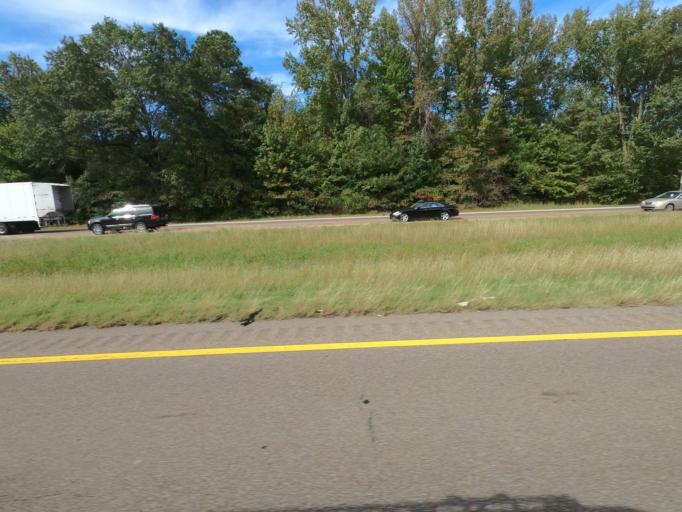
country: US
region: Tennessee
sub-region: Shelby County
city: Lakeland
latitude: 35.2458
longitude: -89.6963
